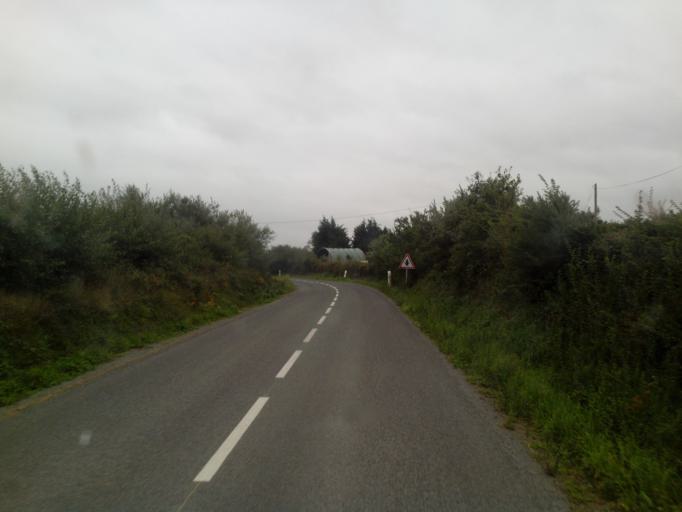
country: FR
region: Brittany
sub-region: Departement des Cotes-d'Armor
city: Pleubian
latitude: 48.8514
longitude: -3.1070
